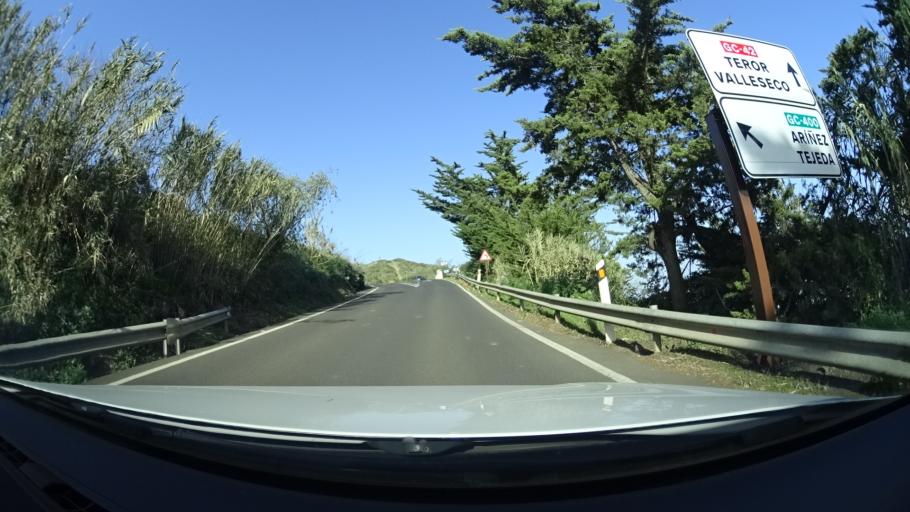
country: ES
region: Canary Islands
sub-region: Provincia de Las Palmas
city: Valleseco
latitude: 28.0289
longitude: -15.5530
